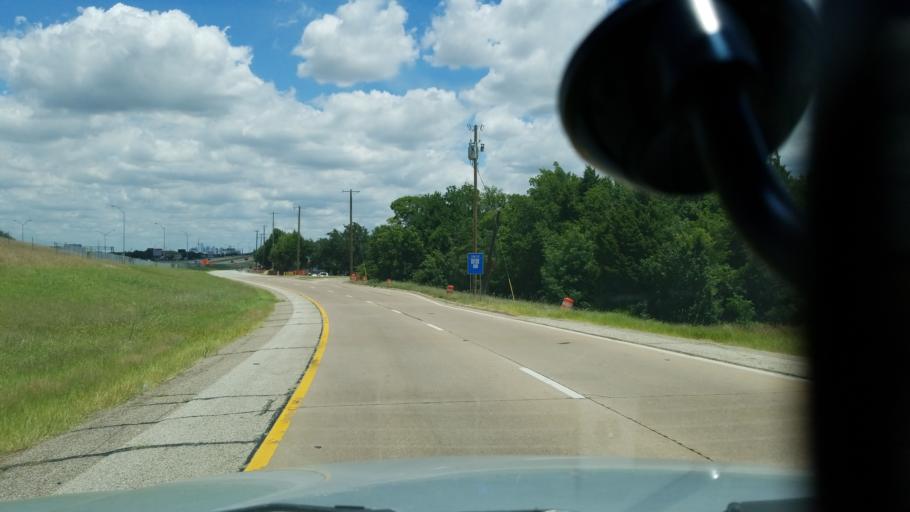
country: US
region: Texas
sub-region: Dallas County
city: Duncanville
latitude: 32.6548
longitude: -96.8749
